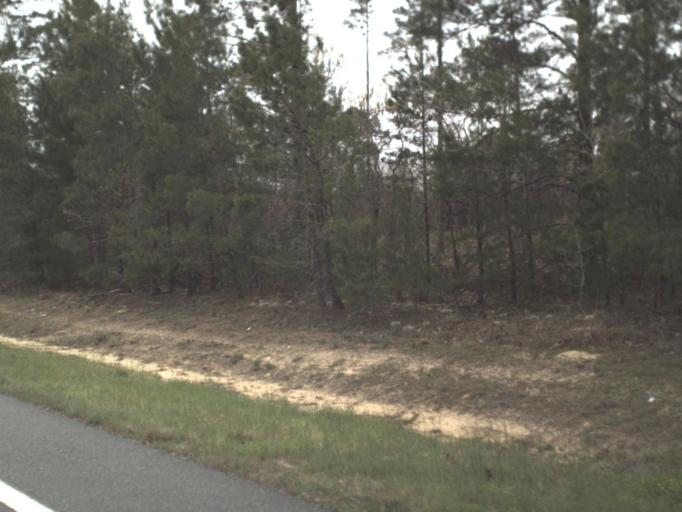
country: US
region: Florida
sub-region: Calhoun County
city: Blountstown
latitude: 30.3828
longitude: -85.2149
